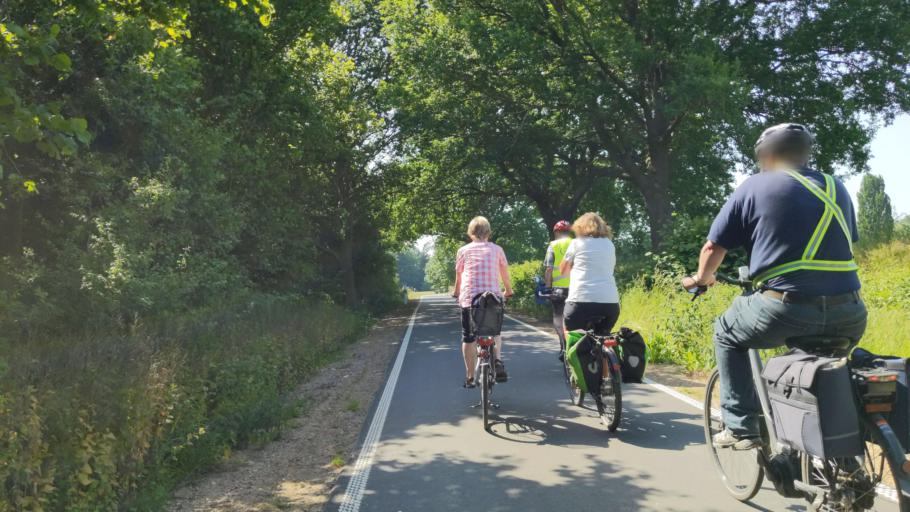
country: DE
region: Schleswig-Holstein
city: Krummesse
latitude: 53.7834
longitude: 10.6342
